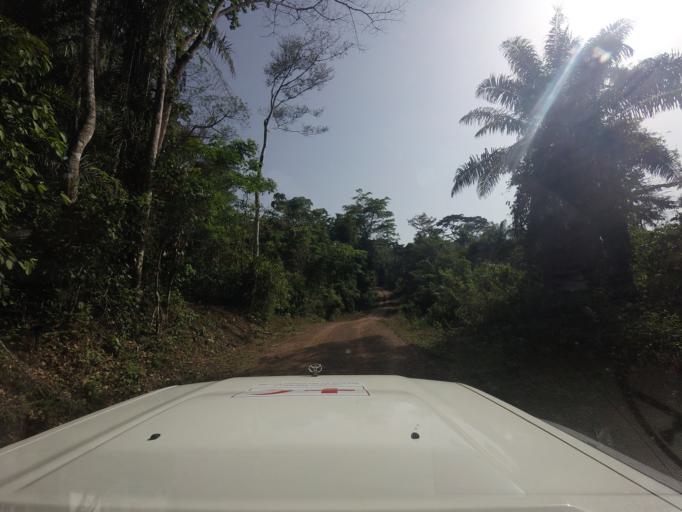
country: LR
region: Lofa
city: Voinjama
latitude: 8.5201
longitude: -9.7592
